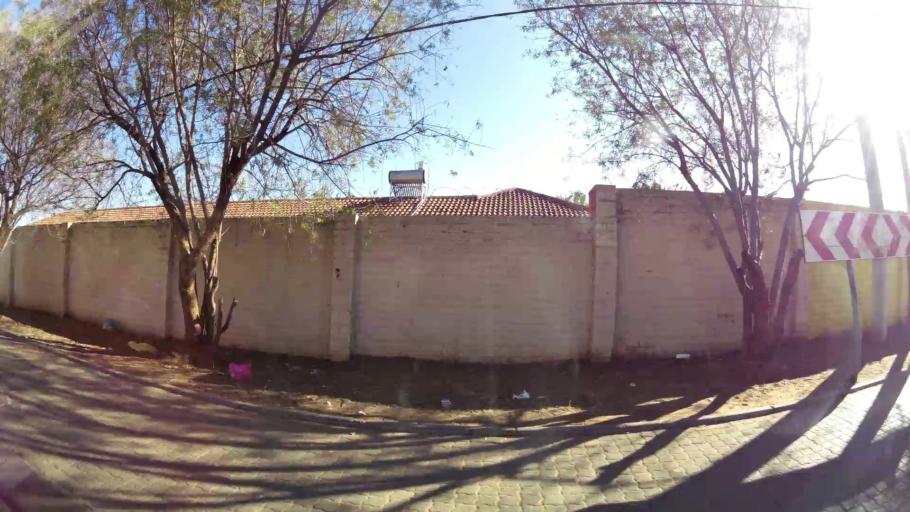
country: ZA
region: Gauteng
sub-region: City of Johannesburg Metropolitan Municipality
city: Roodepoort
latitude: -26.2174
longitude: 27.9417
